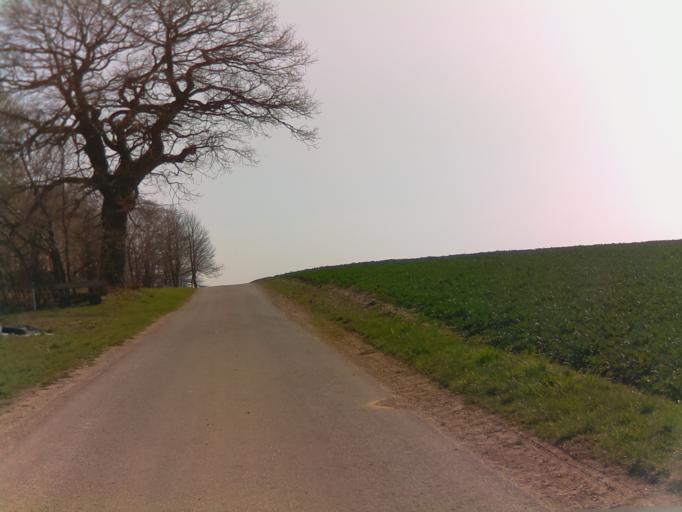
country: DE
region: Rheinland-Pfalz
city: Schwollen
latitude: 49.6973
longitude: 7.1697
